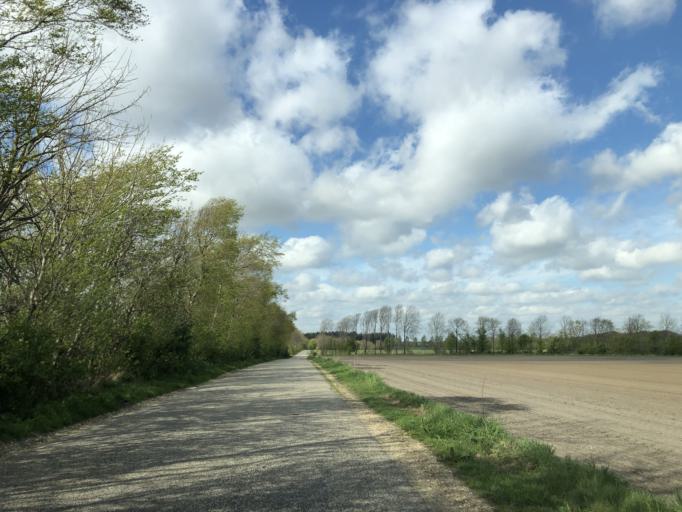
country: DK
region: Central Jutland
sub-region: Herning Kommune
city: Avlum
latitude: 56.2901
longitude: 8.6985
